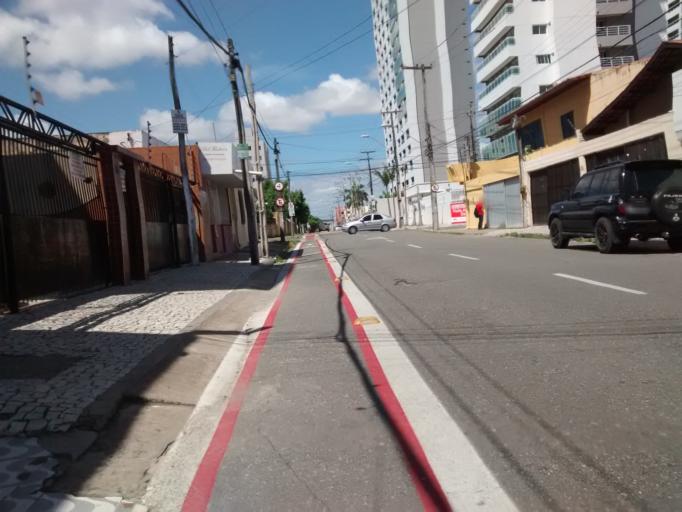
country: BR
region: Ceara
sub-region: Fortaleza
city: Fortaleza
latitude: -3.7352
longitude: -38.5585
